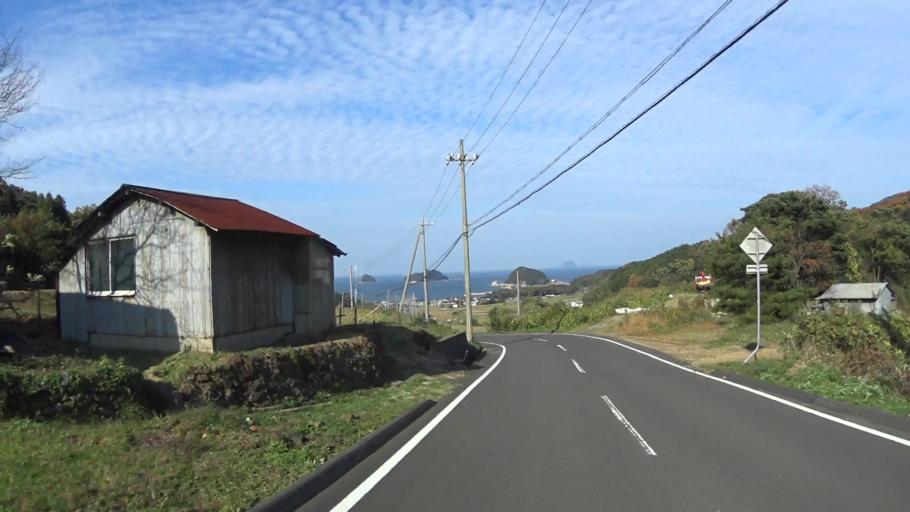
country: JP
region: Kyoto
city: Maizuru
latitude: 35.5506
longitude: 135.3959
